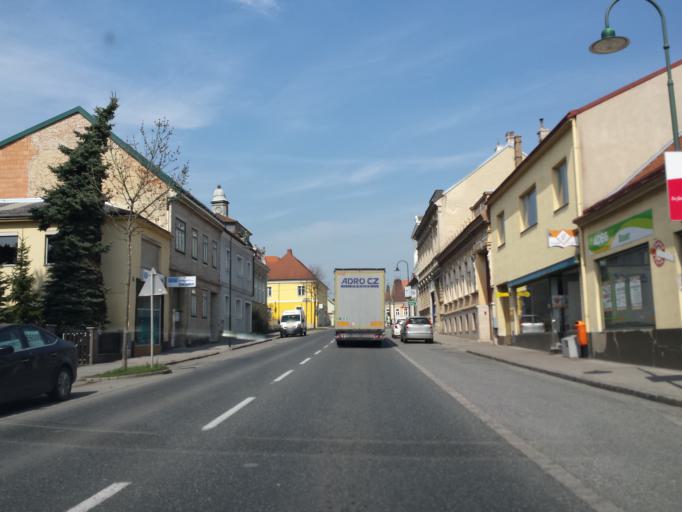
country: AT
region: Lower Austria
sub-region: Politischer Bezirk Mistelbach
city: Poysdorf
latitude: 48.6653
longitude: 16.6285
